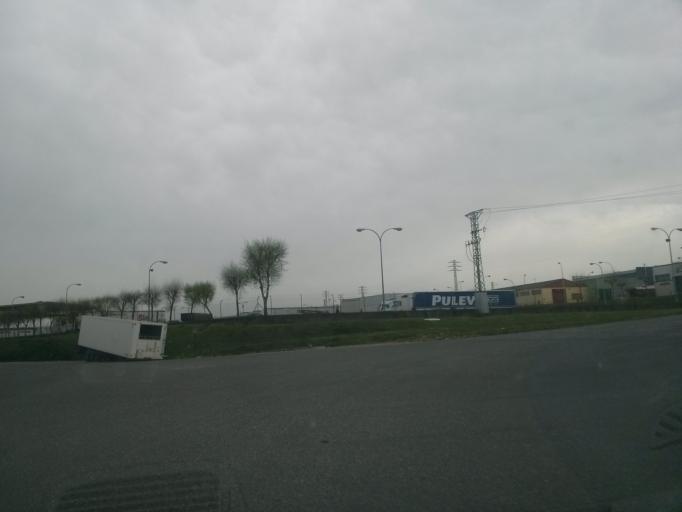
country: ES
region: Galicia
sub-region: Provincia de Lugo
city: Lugo
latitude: 43.0468
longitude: -7.5590
